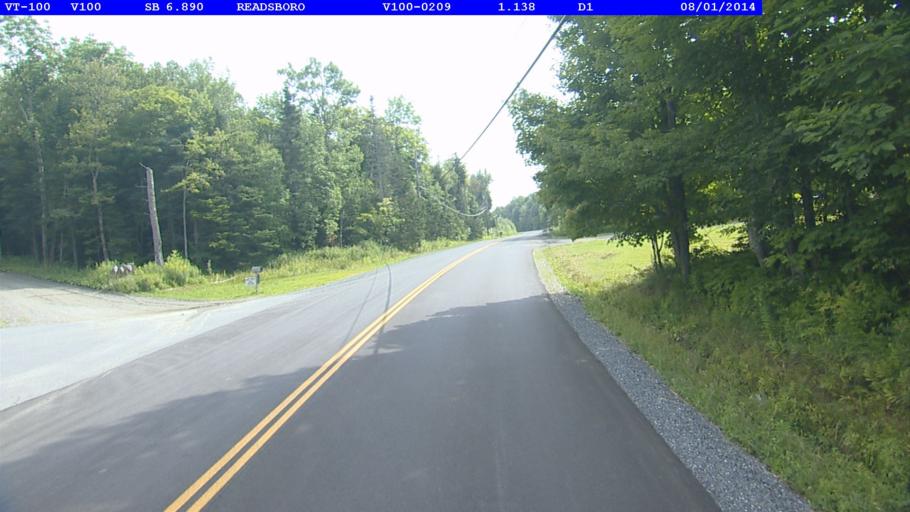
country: US
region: Massachusetts
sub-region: Berkshire County
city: North Adams
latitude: 42.8220
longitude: -73.0040
